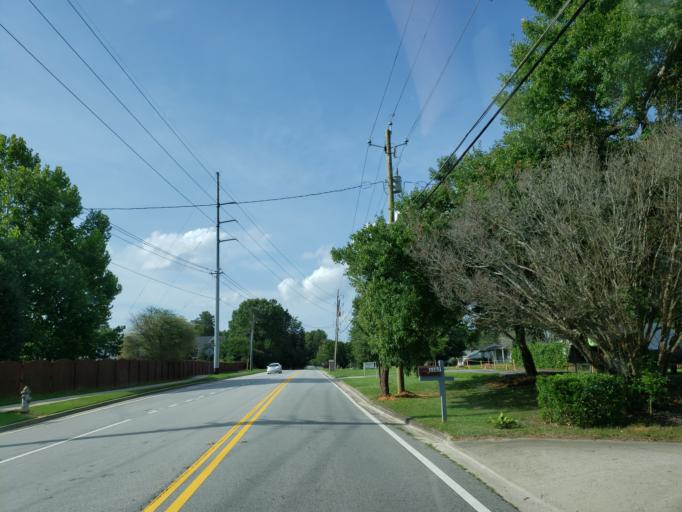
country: US
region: Georgia
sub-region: Cobb County
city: Powder Springs
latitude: 33.8756
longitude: -84.6845
